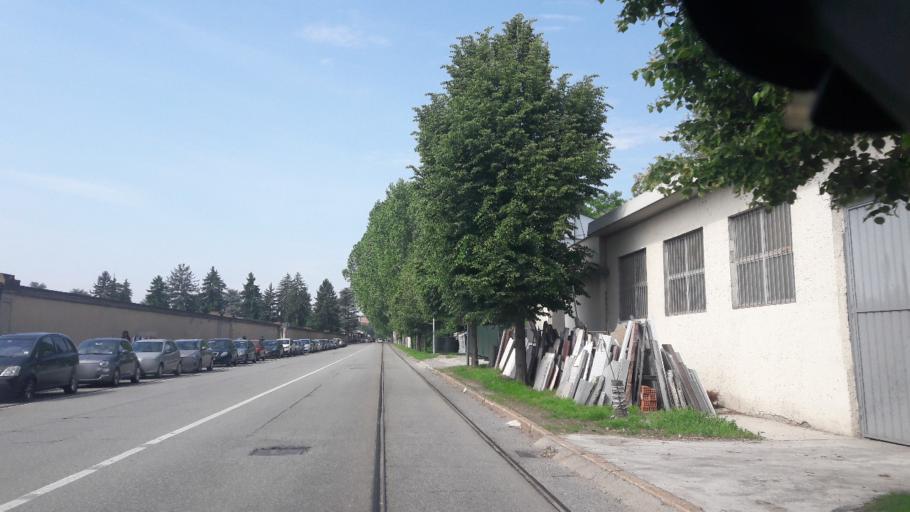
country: IT
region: Piedmont
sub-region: Provincia di Torino
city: Turin
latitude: 45.0837
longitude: 7.7097
